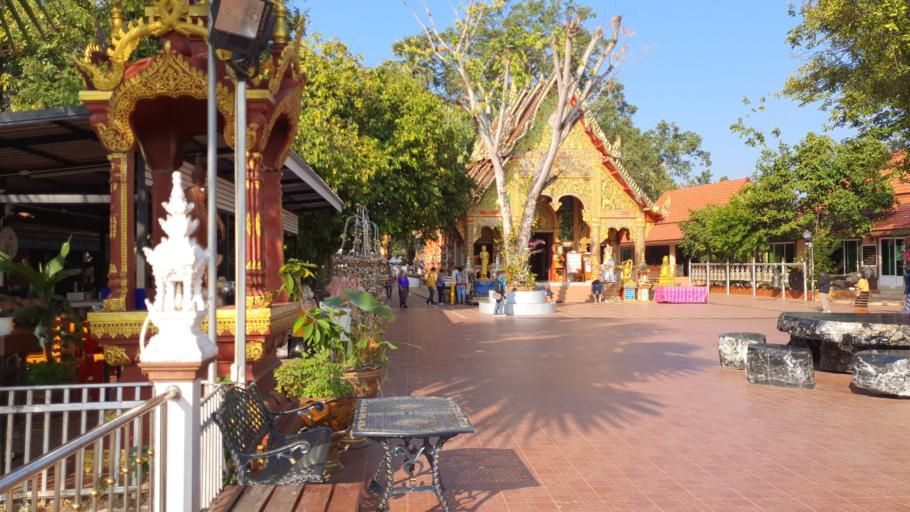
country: TH
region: Nan
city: Pua
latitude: 19.1652
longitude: 100.9344
